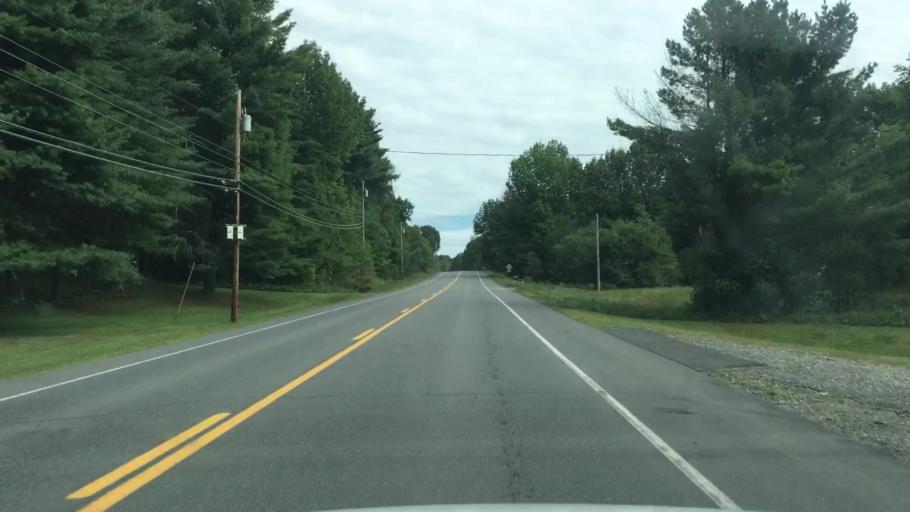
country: US
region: Maine
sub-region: Piscataquis County
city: Dover-Foxcroft
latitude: 45.2090
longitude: -69.1768
